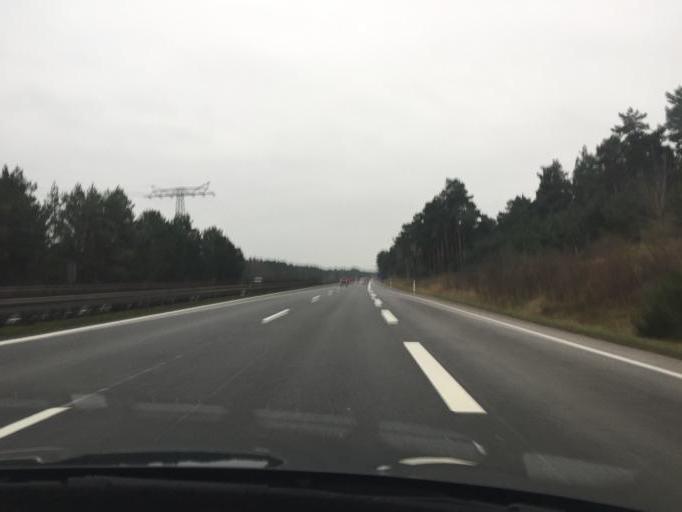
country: DE
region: Brandenburg
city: Schwerin
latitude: 52.1540
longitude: 13.6487
